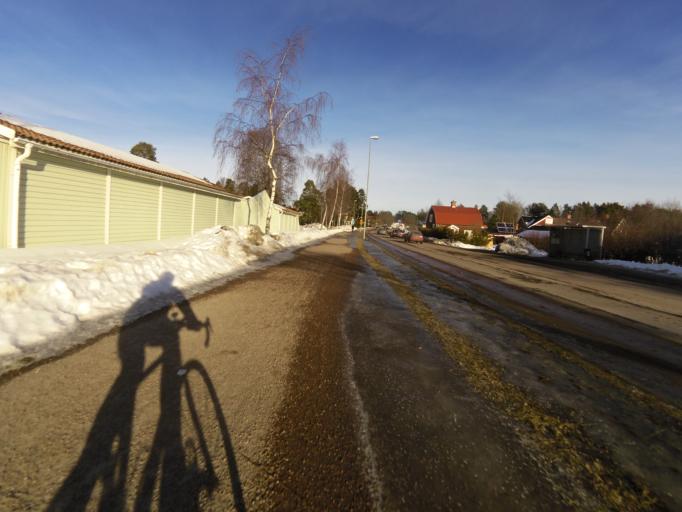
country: SE
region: Gaevleborg
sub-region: Gavle Kommun
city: Valbo
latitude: 60.6464
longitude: 17.0141
